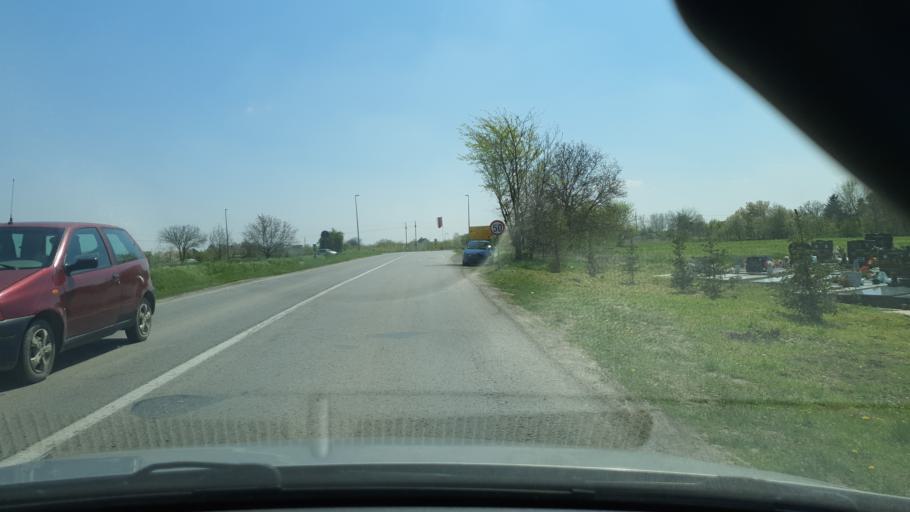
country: RS
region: Autonomna Pokrajina Vojvodina
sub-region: Zapadnobacki Okrug
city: Odzaci
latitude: 45.5008
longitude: 19.2653
